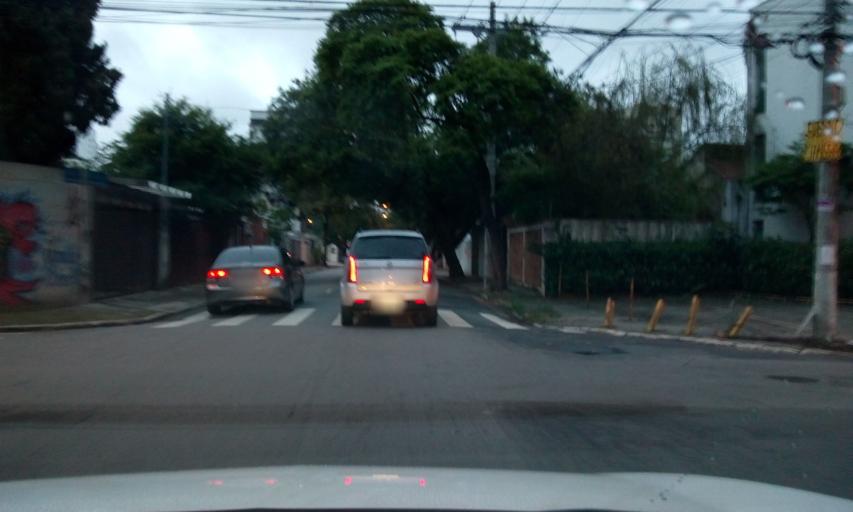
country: BR
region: Sao Paulo
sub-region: Sao Paulo
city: Sao Paulo
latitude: -23.6140
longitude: -46.6889
